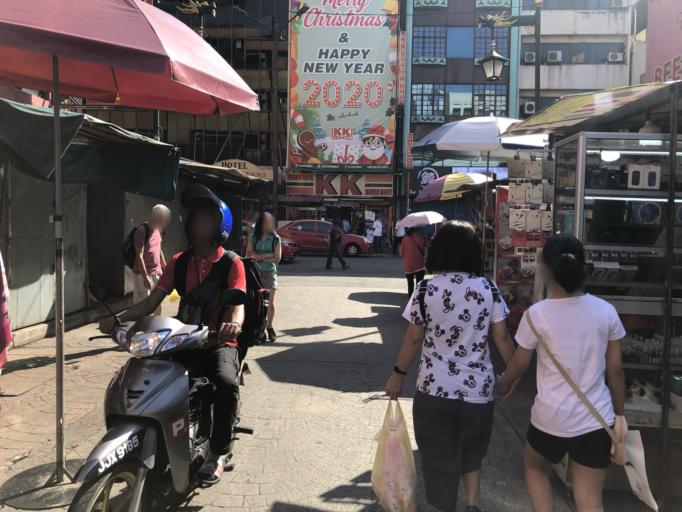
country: MY
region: Kuala Lumpur
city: Kuala Lumpur
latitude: 3.1444
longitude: 101.6985
